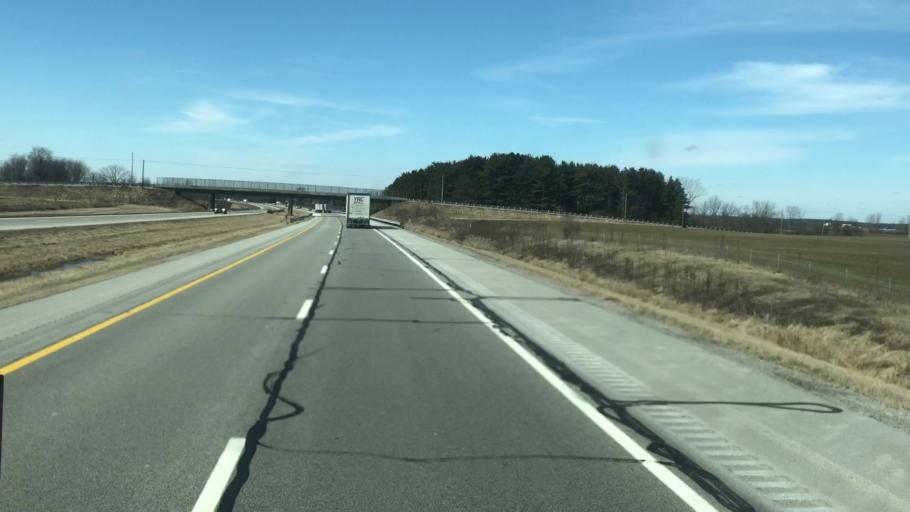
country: US
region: Ohio
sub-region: Williams County
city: Montpelier
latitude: 41.6259
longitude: -84.7056
